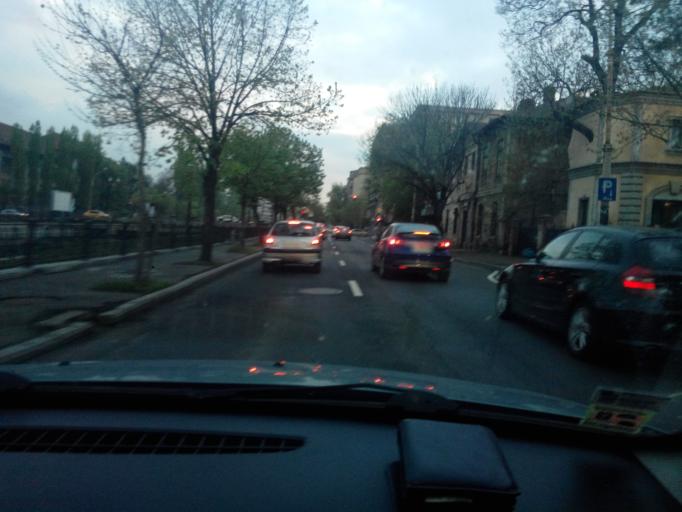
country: RO
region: Bucuresti
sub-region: Municipiul Bucuresti
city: Bucuresti
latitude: 44.4338
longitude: 26.0858
